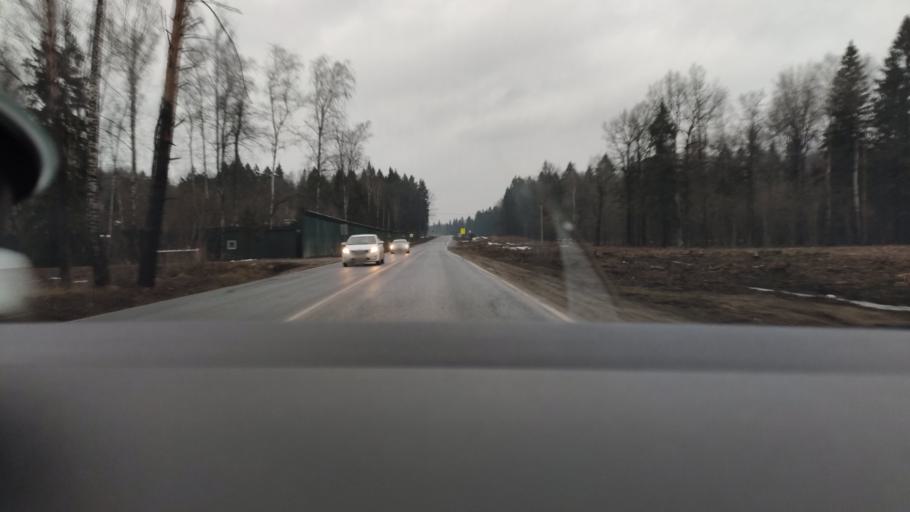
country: RU
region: Moskovskaya
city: Odintsovo
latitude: 55.7000
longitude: 37.2262
